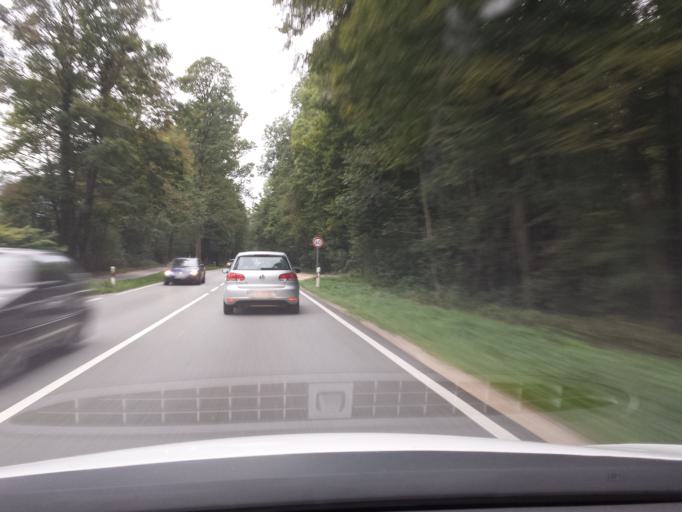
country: DE
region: Bavaria
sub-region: Upper Bavaria
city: Bad Reichenhall
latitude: 47.7398
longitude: 12.8878
